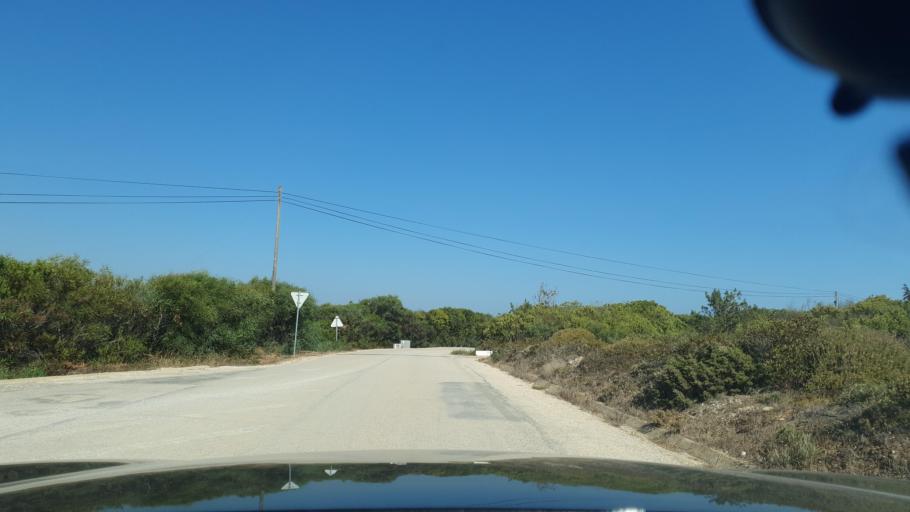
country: PT
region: Beja
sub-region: Odemira
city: Sao Teotonio
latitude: 37.4382
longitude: -8.7969
